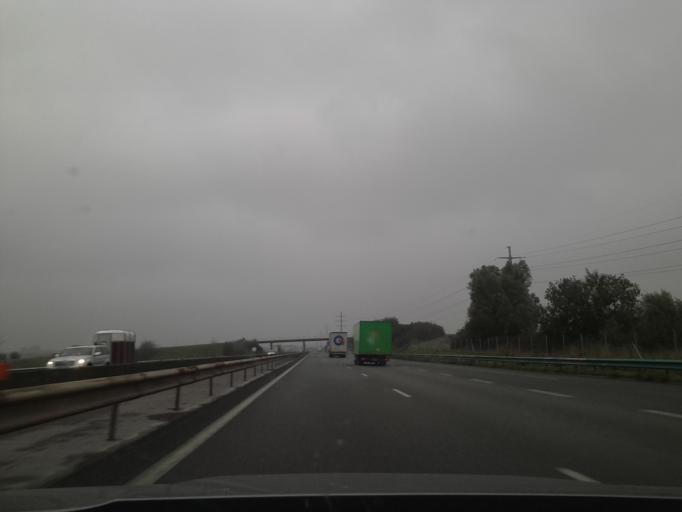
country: FR
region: Nord-Pas-de-Calais
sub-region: Departement du Nord
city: Escaudoeuvres
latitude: 50.2276
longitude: 3.2667
